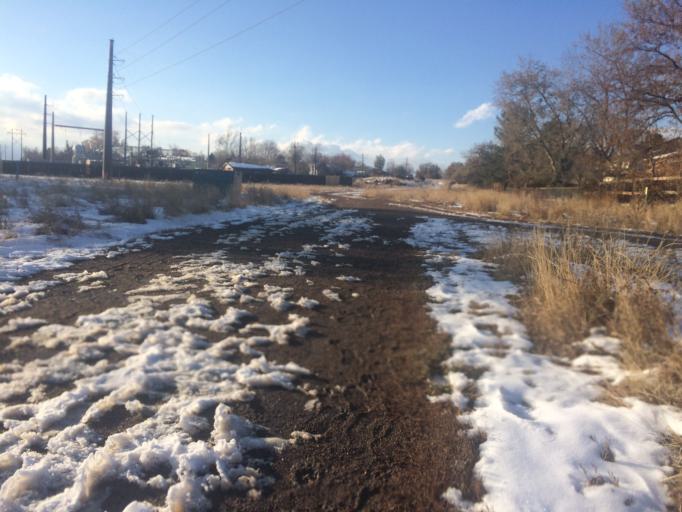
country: US
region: Colorado
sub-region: Boulder County
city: Lafayette
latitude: 39.9905
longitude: -105.1116
